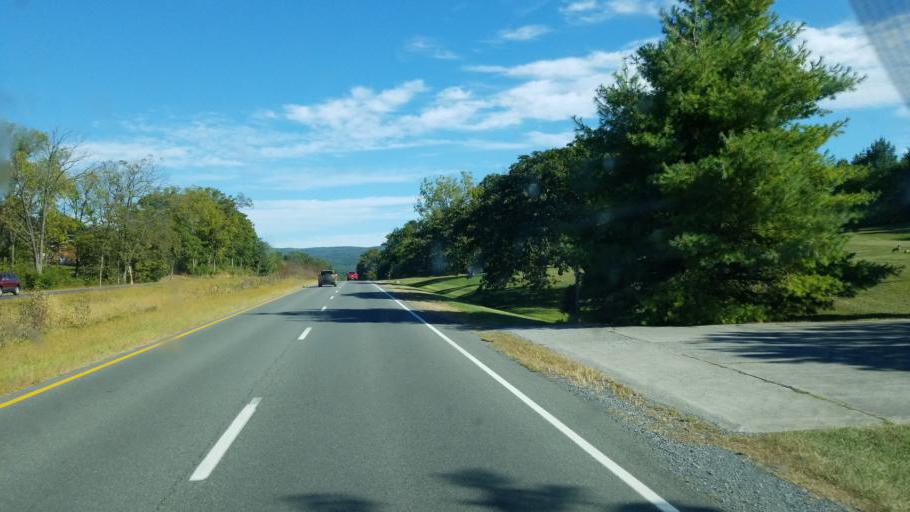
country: US
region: Virginia
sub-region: Warren County
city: Shenandoah Farms
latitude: 39.0537
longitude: -78.0286
